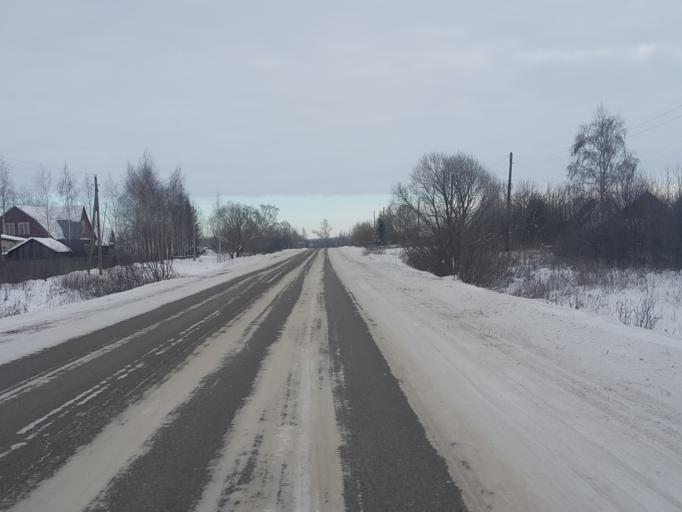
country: RU
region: Tambov
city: Platonovka
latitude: 52.8538
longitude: 41.8200
